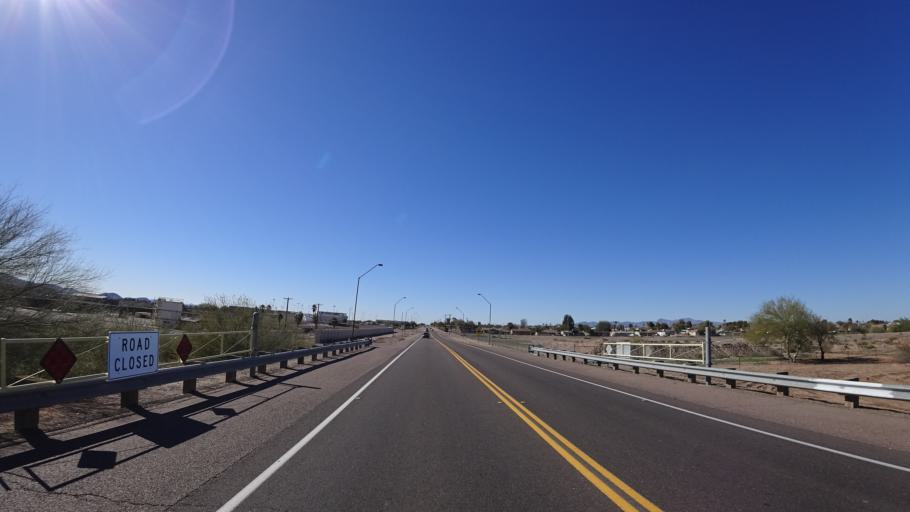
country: US
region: Arizona
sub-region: Maricopa County
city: Avondale
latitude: 33.4208
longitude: -112.3424
